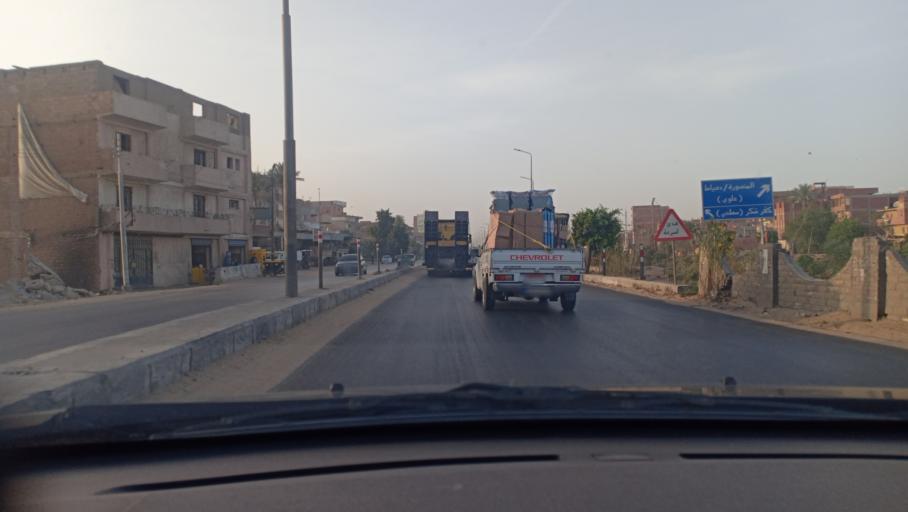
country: EG
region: Muhafazat al Minufiyah
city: Quwaysina
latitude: 30.5436
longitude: 31.2693
